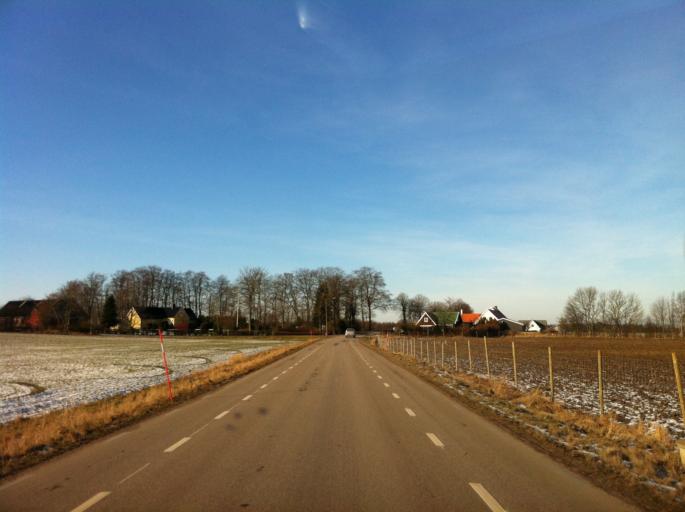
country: SE
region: Skane
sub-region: Angelholms Kommun
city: Strovelstorp
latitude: 56.1081
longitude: 12.7915
